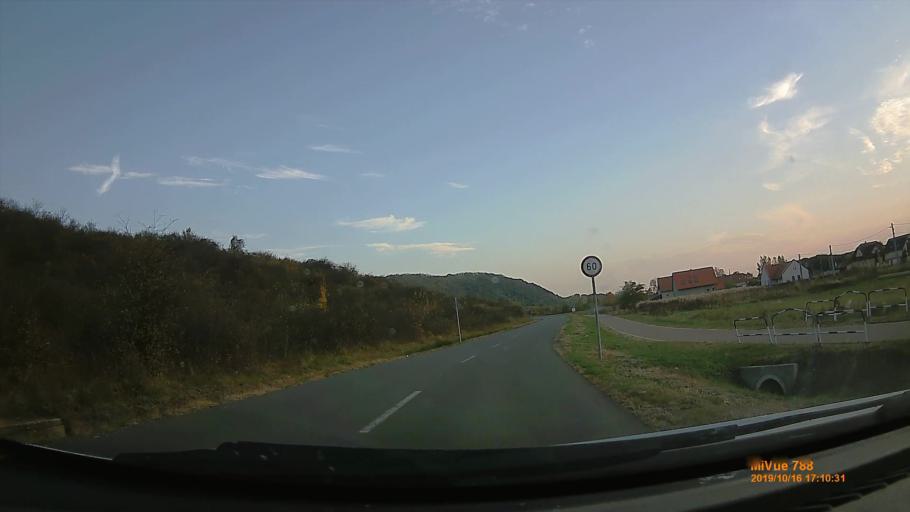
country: HU
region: Heves
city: Egerszalok
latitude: 47.8416
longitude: 20.3340
